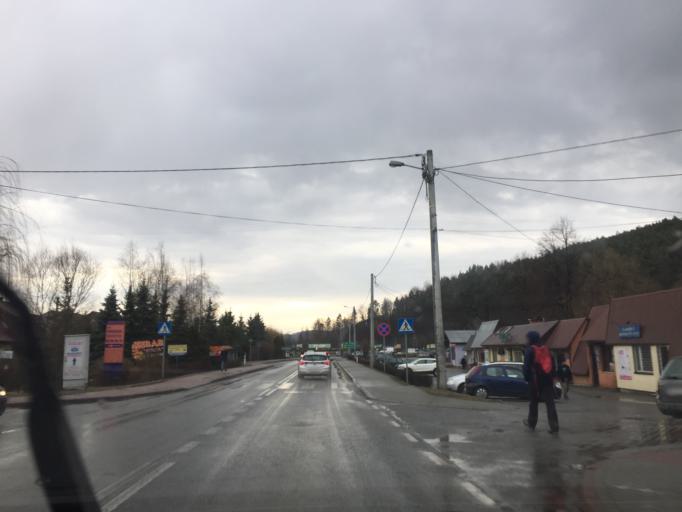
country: PL
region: Lesser Poland Voivodeship
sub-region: Powiat myslenicki
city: Sulkowice
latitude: 49.8548
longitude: 19.7991
